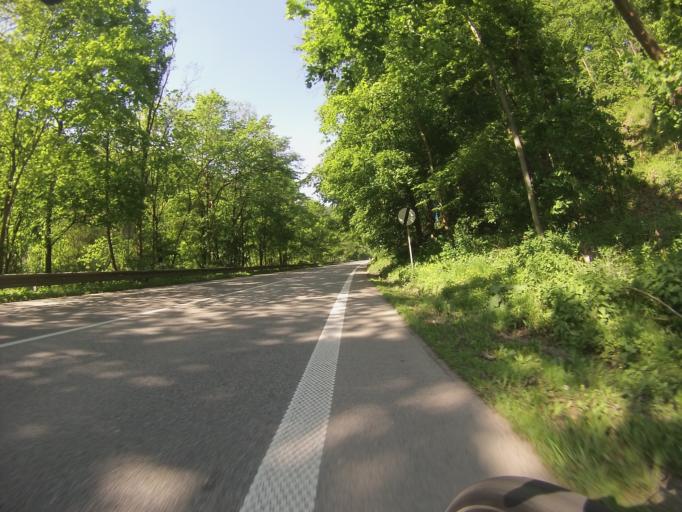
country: CZ
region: South Moravian
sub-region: Okres Blansko
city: Adamov
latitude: 49.3289
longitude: 16.6434
